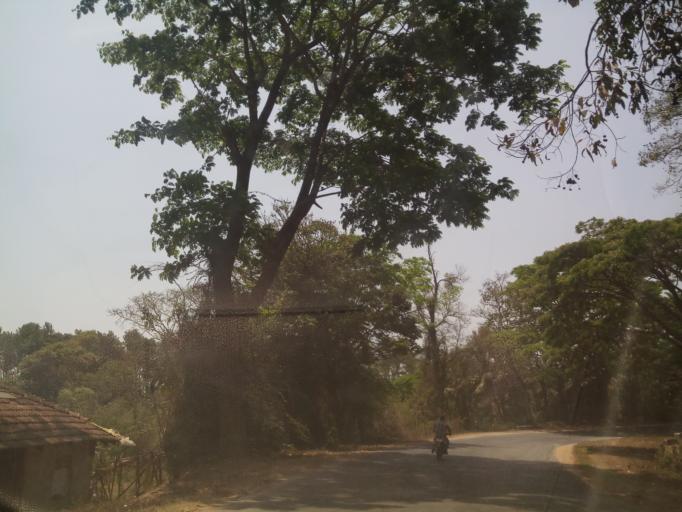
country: IN
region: Karnataka
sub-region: Hassan
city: Sakleshpur
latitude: 12.9554
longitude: 75.8369
